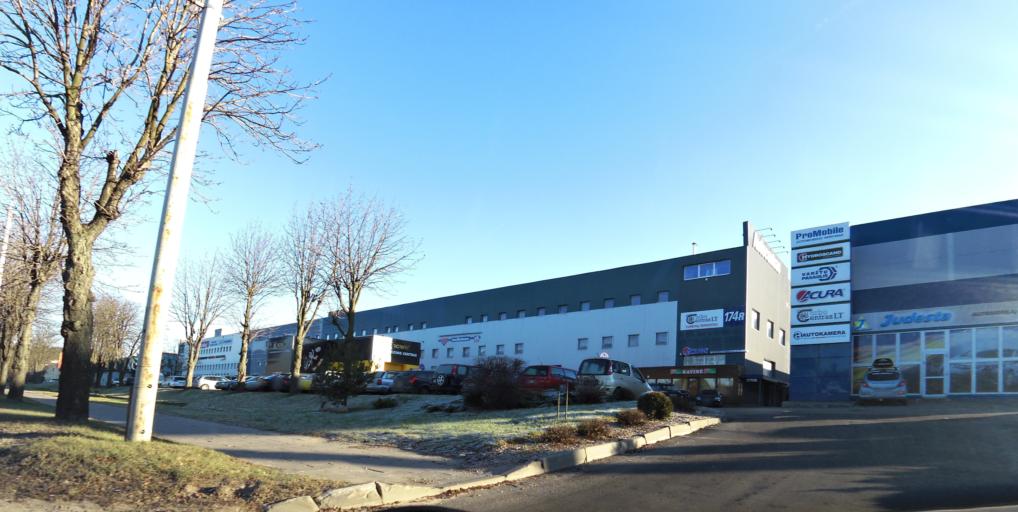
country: LT
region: Vilnius County
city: Lazdynai
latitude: 54.6551
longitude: 25.2261
